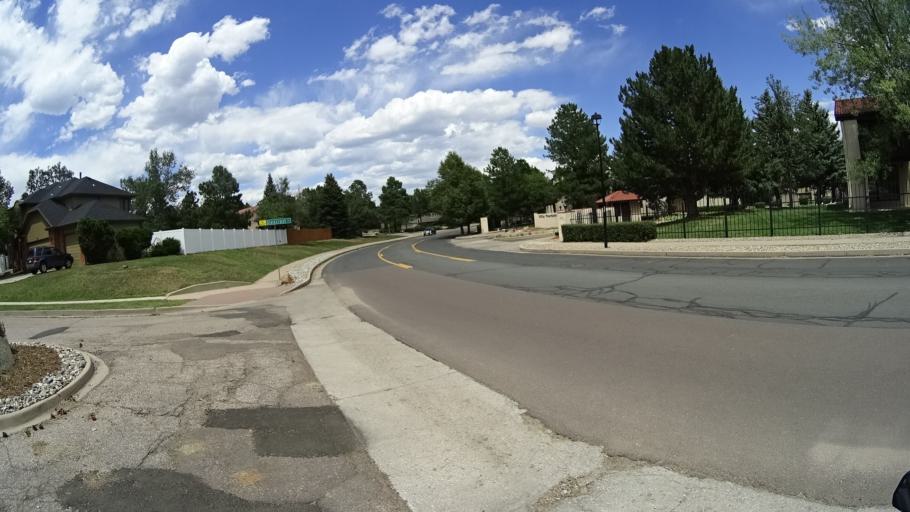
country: US
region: Colorado
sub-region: El Paso County
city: Colorado Springs
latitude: 38.7873
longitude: -104.8249
